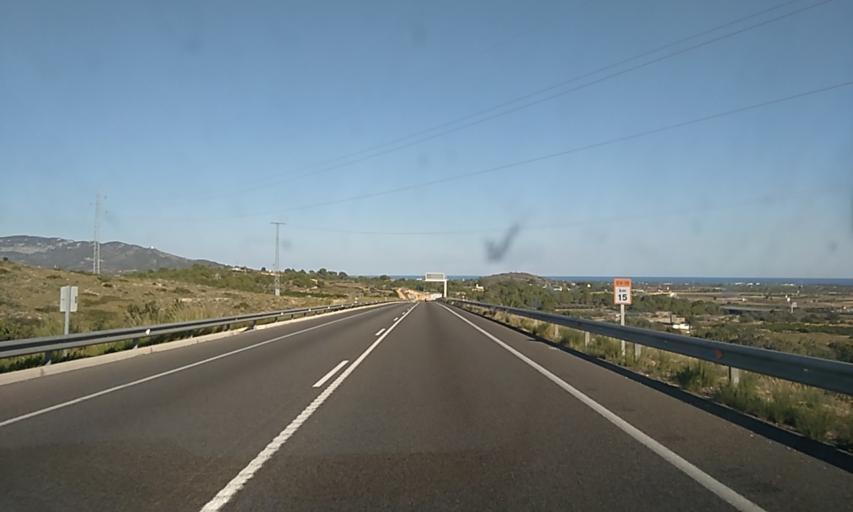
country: ES
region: Valencia
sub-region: Provincia de Castello
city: Torreblanca
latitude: 40.2311
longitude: 0.1978
